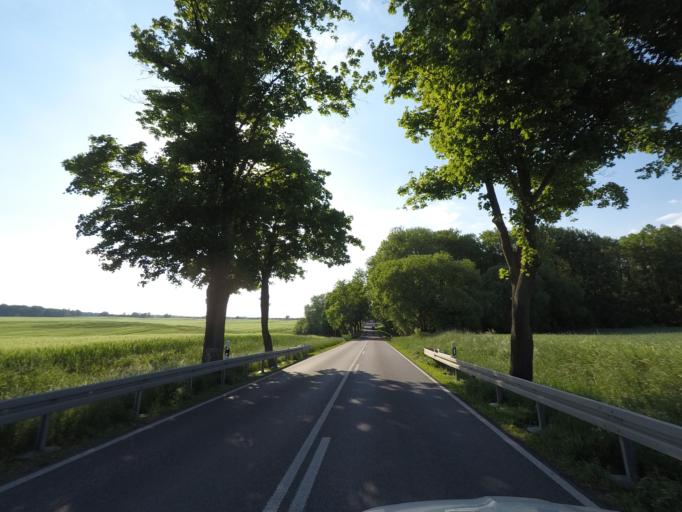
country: DE
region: Brandenburg
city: Hohenfinow
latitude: 52.8142
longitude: 13.9139
